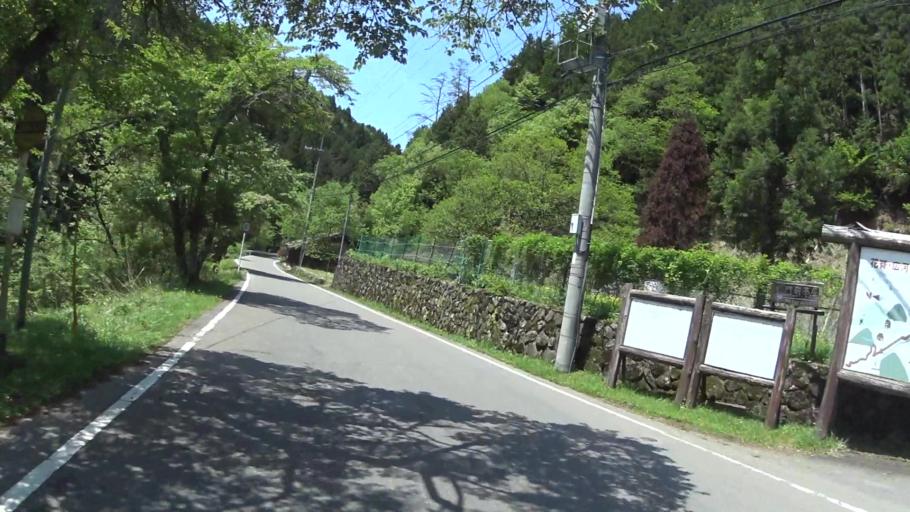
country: JP
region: Shiga Prefecture
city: Kitahama
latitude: 35.2074
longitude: 135.7794
